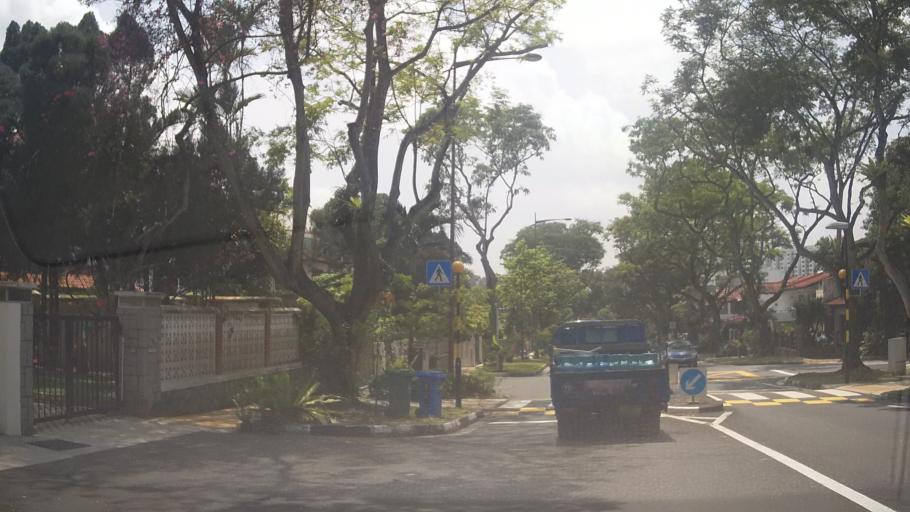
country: SG
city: Singapore
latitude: 1.3155
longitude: 103.7836
